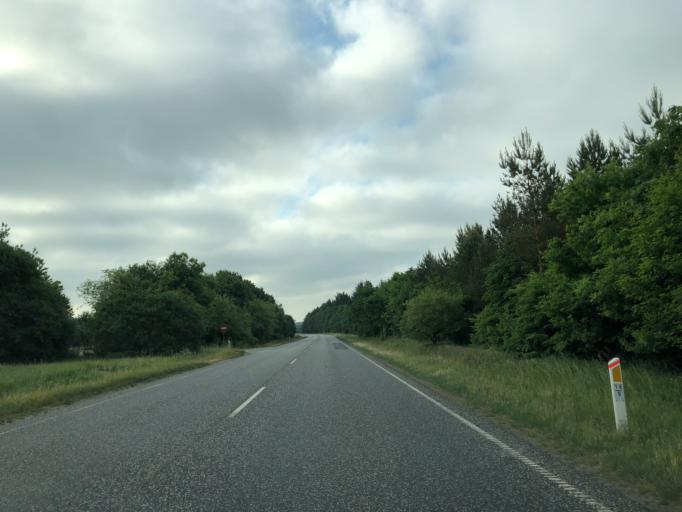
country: DK
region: South Denmark
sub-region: Vejle Kommune
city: Give
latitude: 55.7595
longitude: 9.2985
